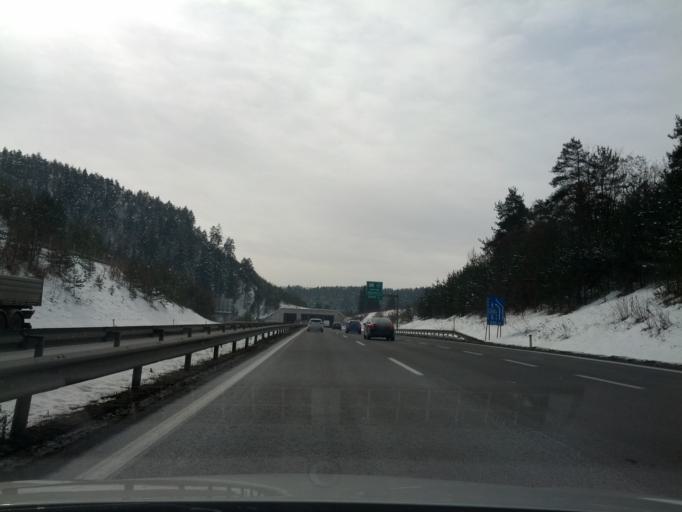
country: SI
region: Skofljica
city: Lavrica
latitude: 46.0337
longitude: 14.5712
